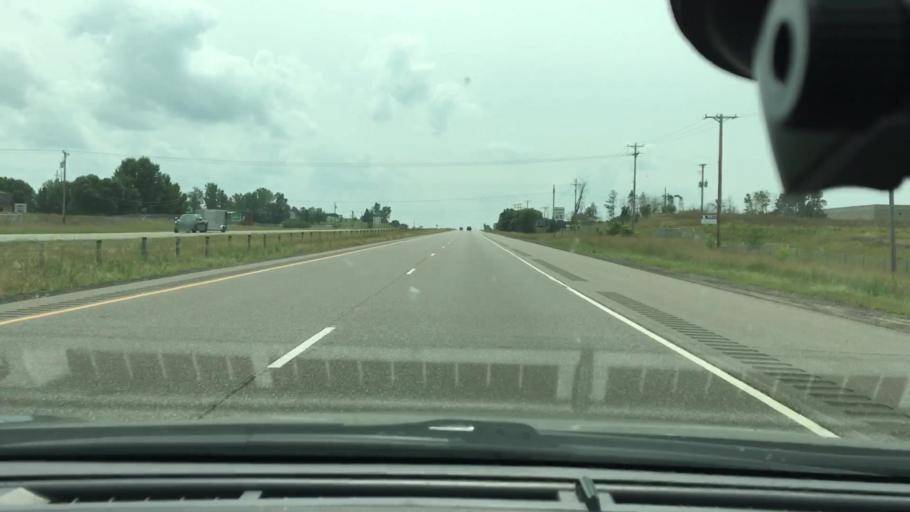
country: US
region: Minnesota
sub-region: Hennepin County
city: Rogers
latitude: 45.2216
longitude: -93.5527
